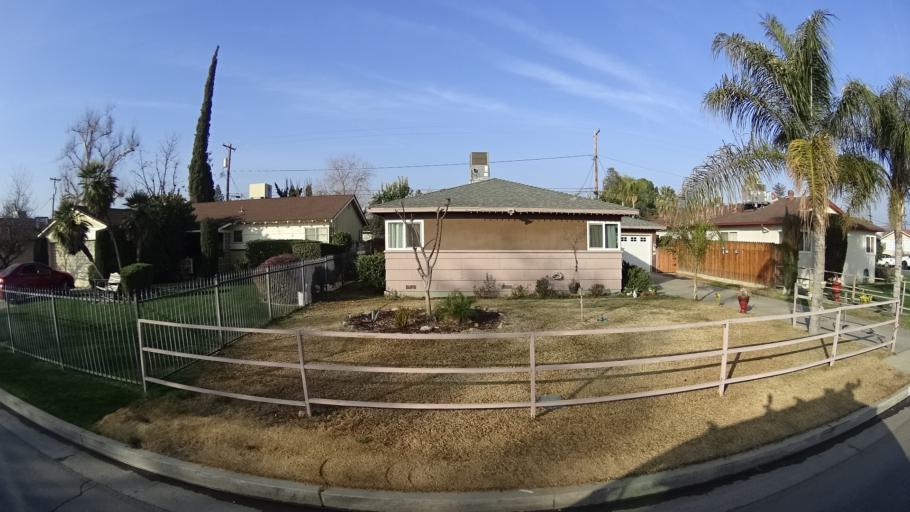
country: US
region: California
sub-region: Kern County
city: Bakersfield
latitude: 35.3381
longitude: -119.0282
